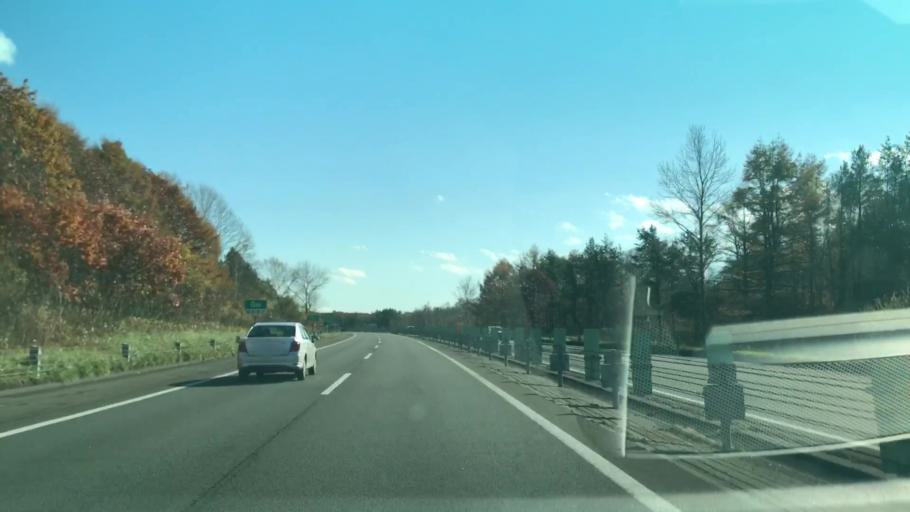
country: JP
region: Hokkaido
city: Chitose
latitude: 42.8567
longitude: 141.5626
